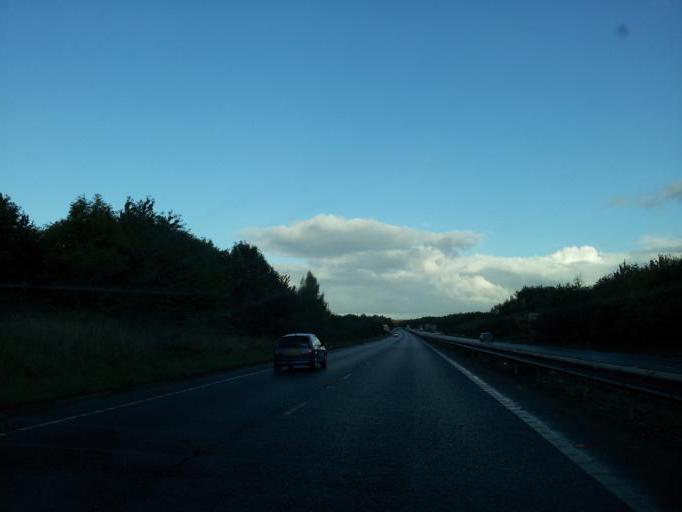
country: GB
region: England
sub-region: Norfolk
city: Cringleford
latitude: 52.6102
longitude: 1.2174
